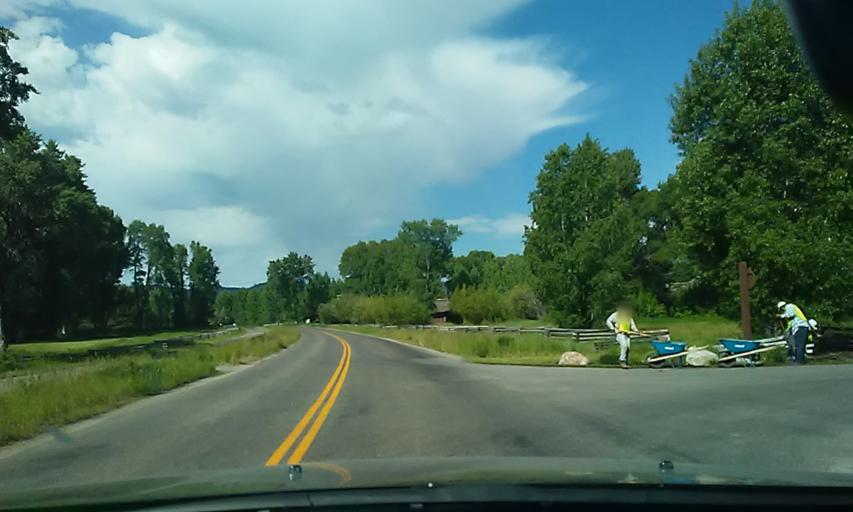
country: US
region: Wyoming
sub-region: Teton County
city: Jackson
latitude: 43.5670
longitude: -110.7457
